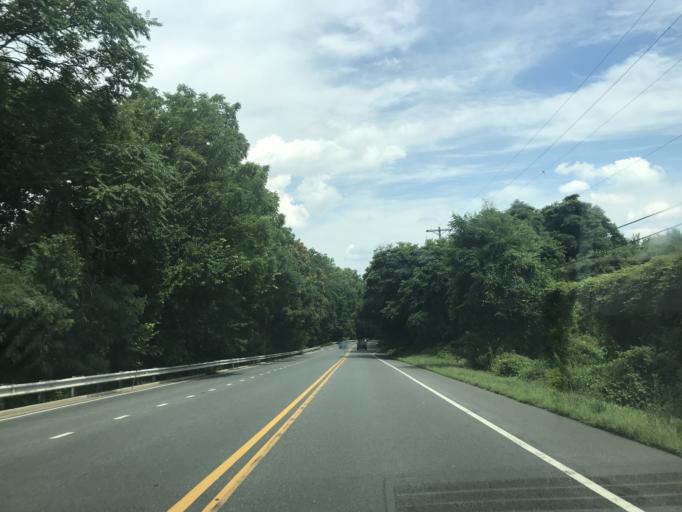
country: US
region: Delaware
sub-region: New Castle County
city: Greenville
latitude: 39.7643
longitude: -75.6483
